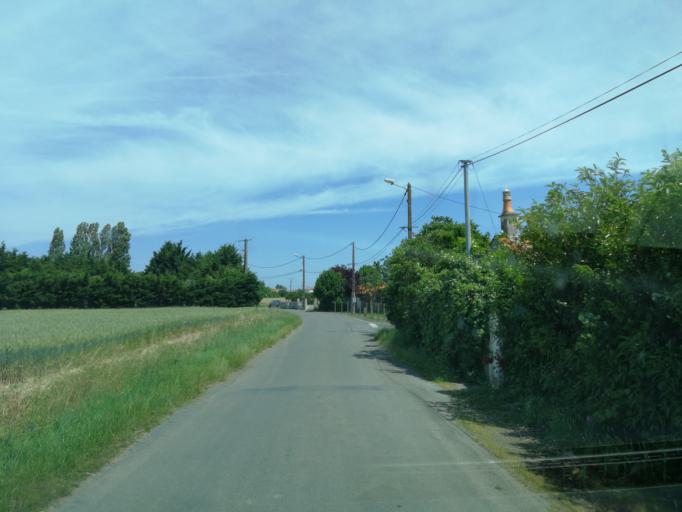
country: FR
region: Pays de la Loire
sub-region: Departement de la Vendee
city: Le Langon
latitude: 46.3814
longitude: -0.9436
